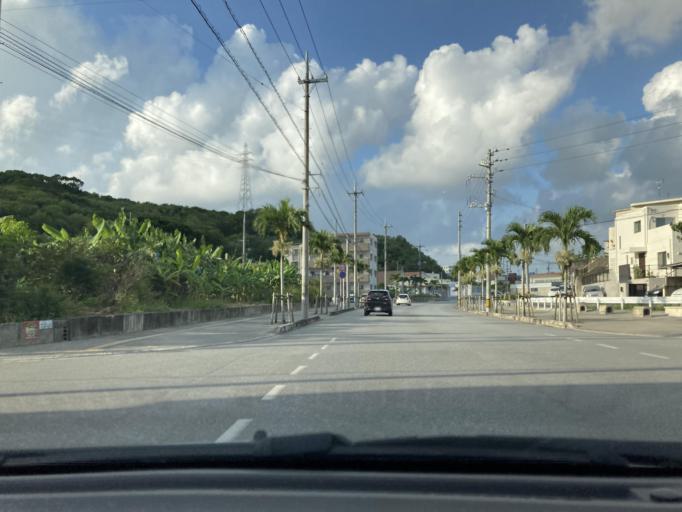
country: JP
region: Okinawa
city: Tomigusuku
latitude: 26.1530
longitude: 127.7175
